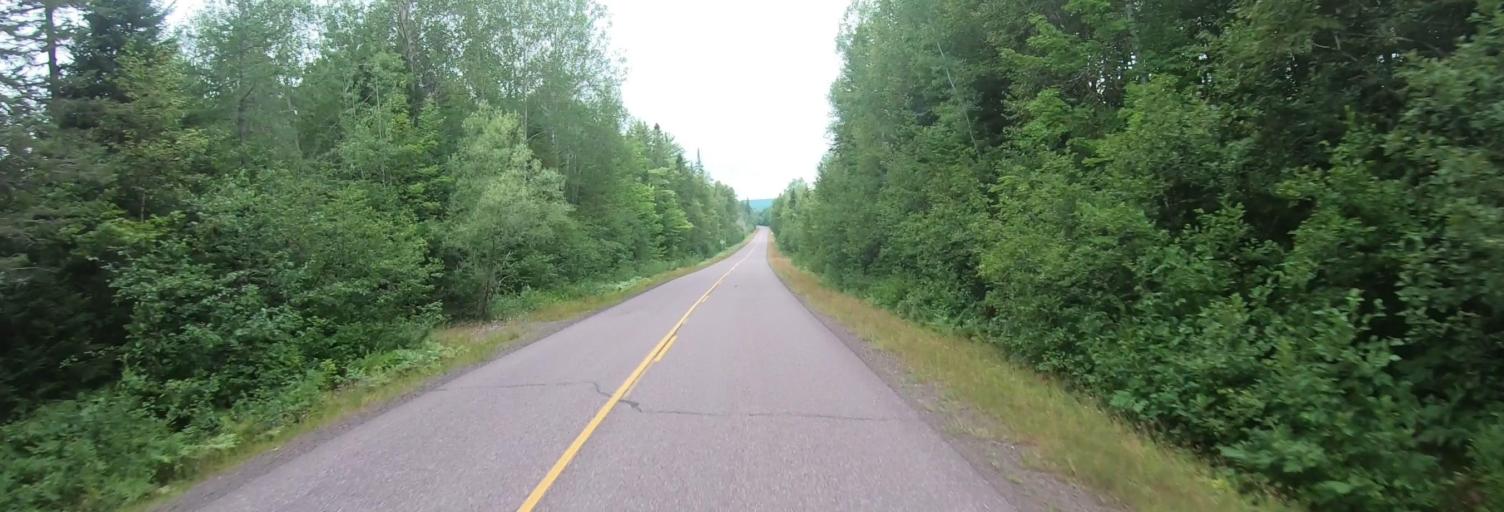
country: US
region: Michigan
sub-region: Keweenaw County
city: Eagle River
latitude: 47.2820
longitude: -88.2758
